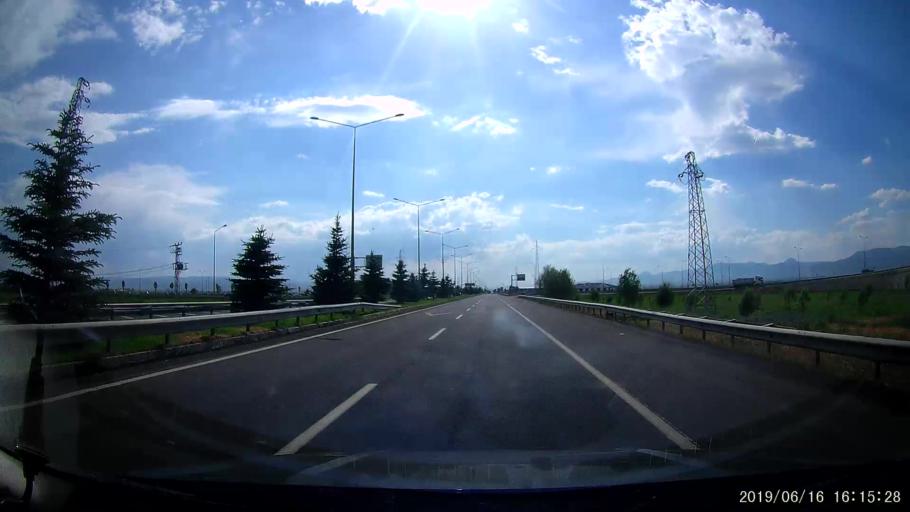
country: TR
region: Erzurum
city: Erzurum
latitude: 39.9619
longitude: 41.2256
